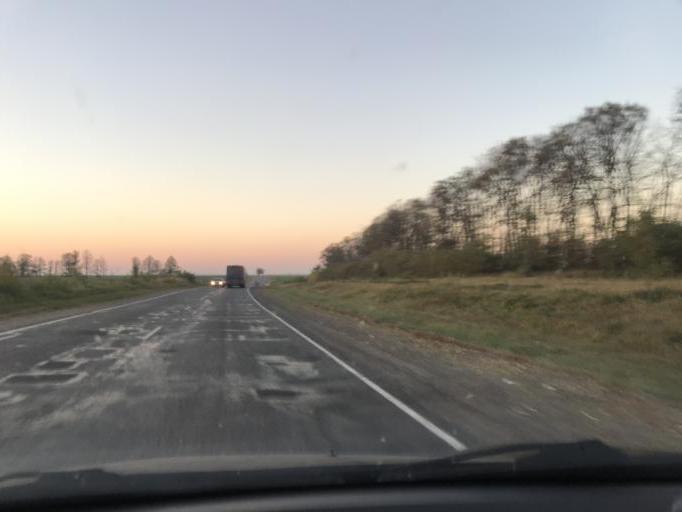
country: BY
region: Gomel
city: Horad Rechytsa
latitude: 52.2145
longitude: 30.5263
